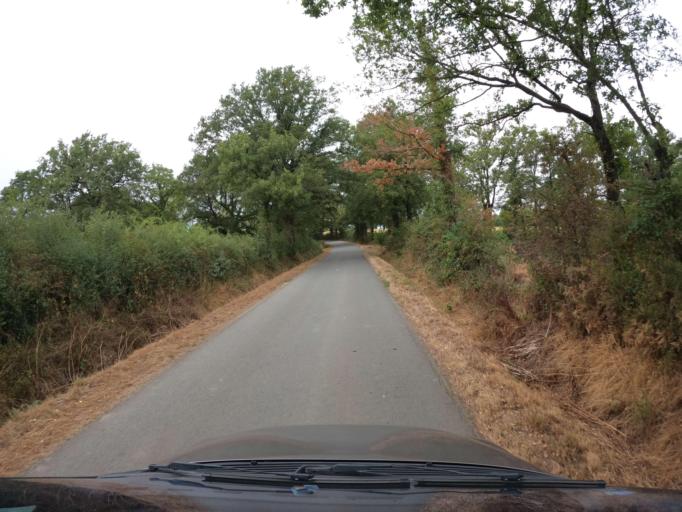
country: FR
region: Pays de la Loire
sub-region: Departement de Maine-et-Loire
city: La Romagne
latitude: 47.0488
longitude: -0.9962
